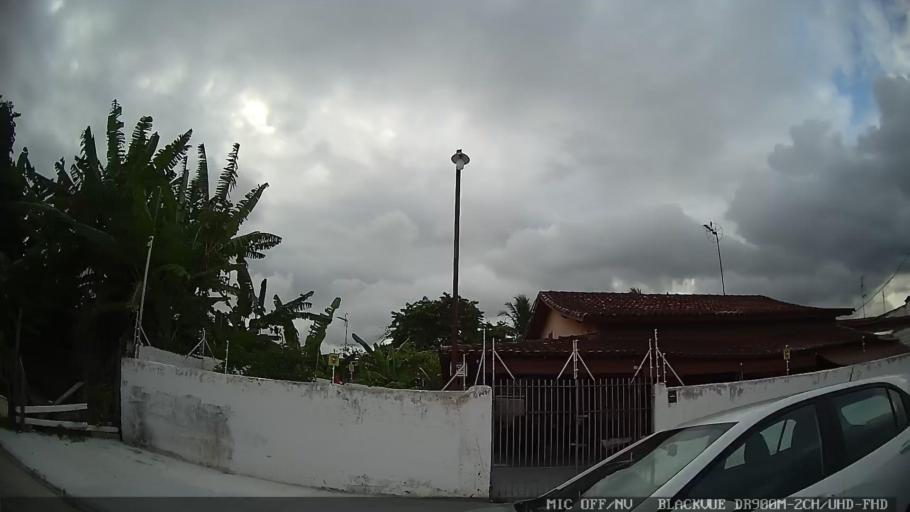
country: BR
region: Sao Paulo
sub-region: Caraguatatuba
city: Caraguatatuba
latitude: -23.6399
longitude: -45.4291
